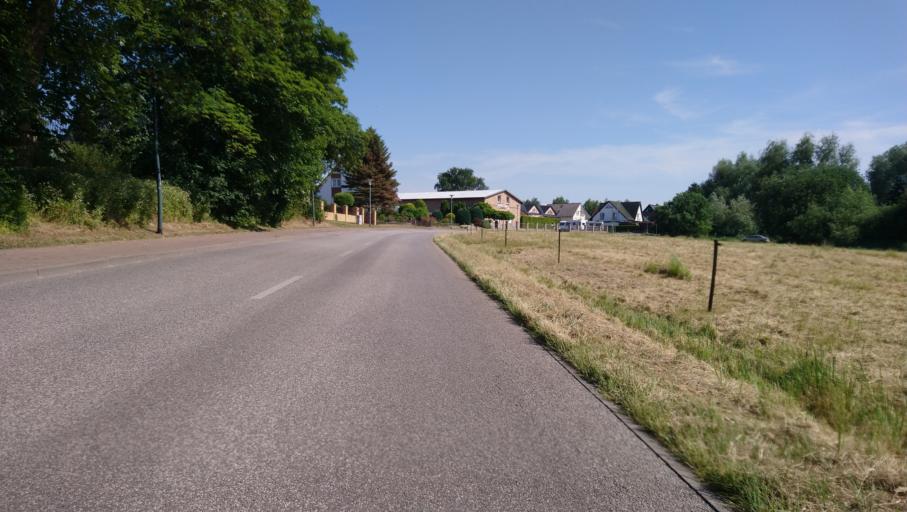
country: DE
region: Mecklenburg-Vorpommern
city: Dierkow-Neu
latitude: 54.0913
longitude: 12.1855
